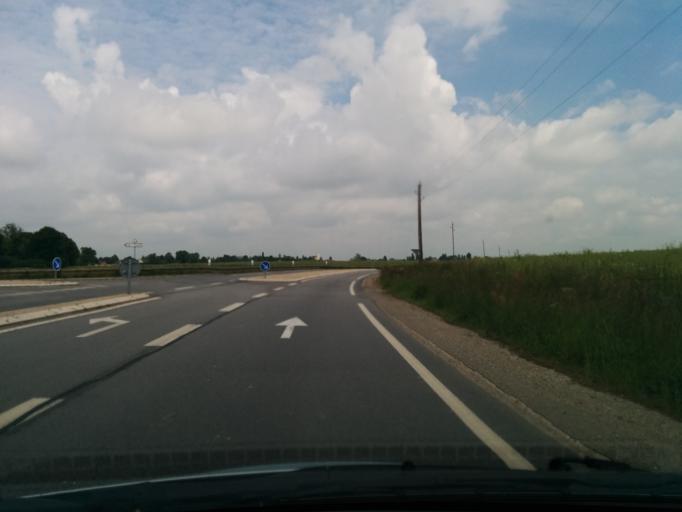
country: FR
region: Haute-Normandie
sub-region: Departement de l'Eure
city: Vernon
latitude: 49.1363
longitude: 1.5211
